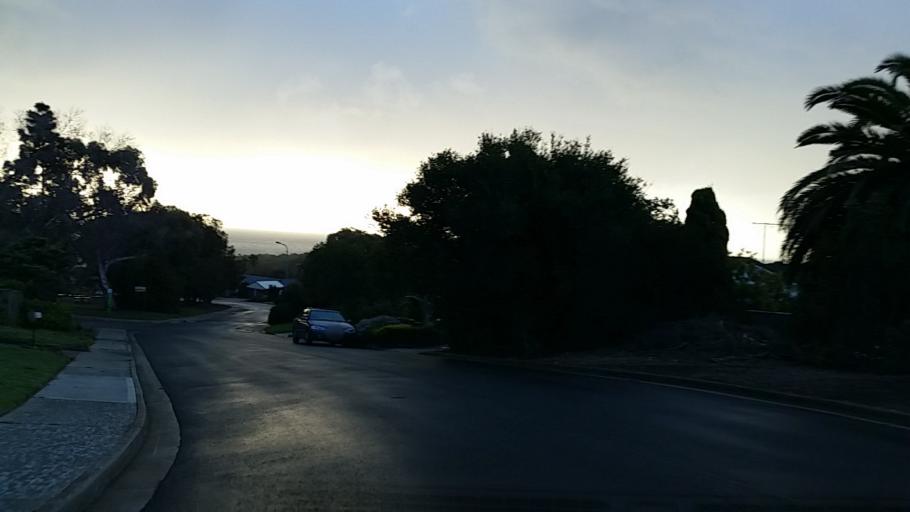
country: AU
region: South Australia
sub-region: Marion
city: Happy Valley
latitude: -35.0740
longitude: 138.5086
